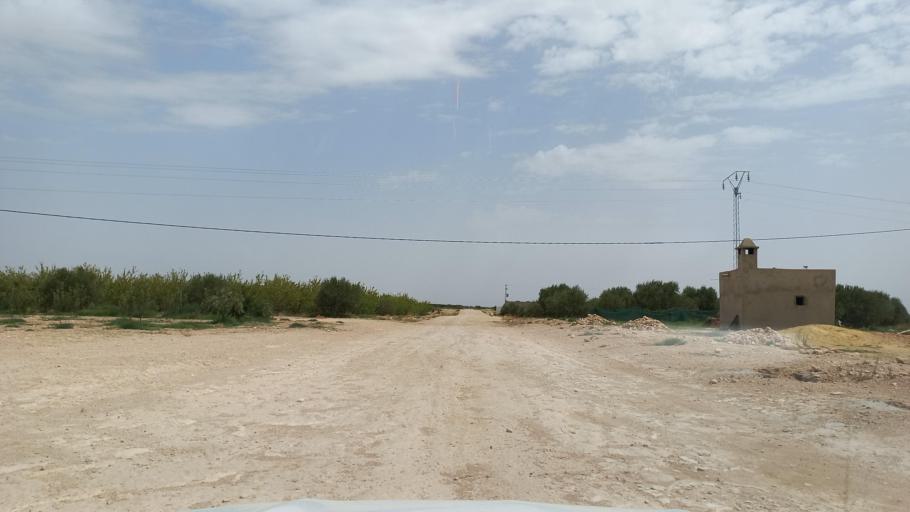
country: TN
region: Al Qasrayn
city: Kasserine
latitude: 35.2818
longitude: 9.0074
